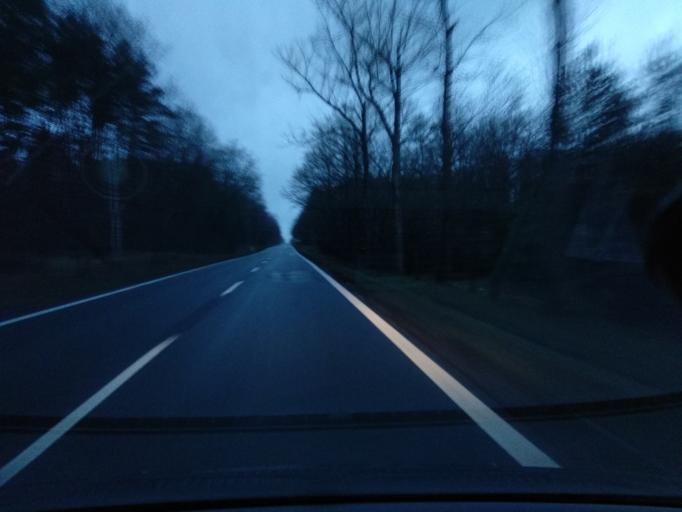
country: PL
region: Lower Silesian Voivodeship
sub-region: Powiat legnicki
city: Prochowice
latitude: 51.2454
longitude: 16.4090
